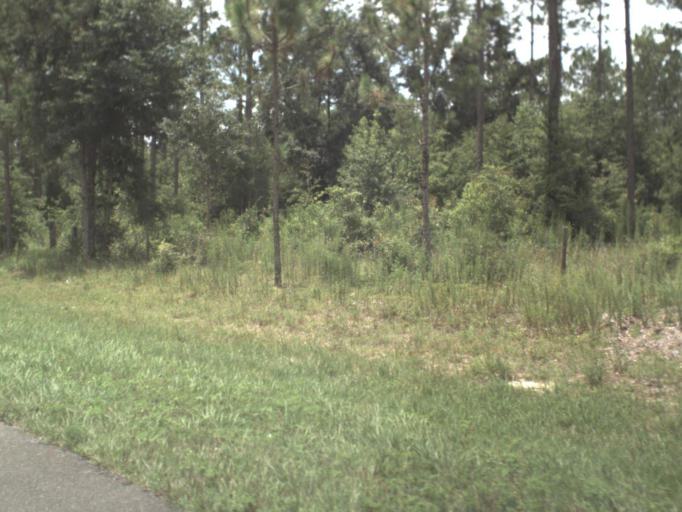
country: US
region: Florida
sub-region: Levy County
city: Williston
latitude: 29.4601
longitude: -82.4766
